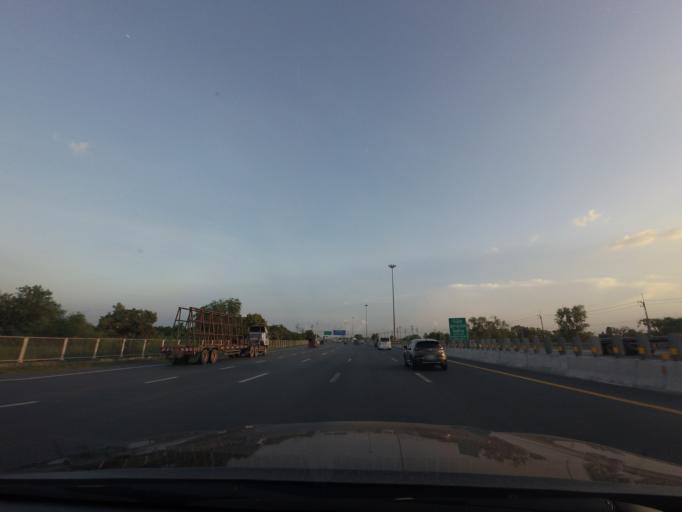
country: TH
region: Pathum Thani
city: Thanyaburi
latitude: 14.0225
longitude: 100.6988
